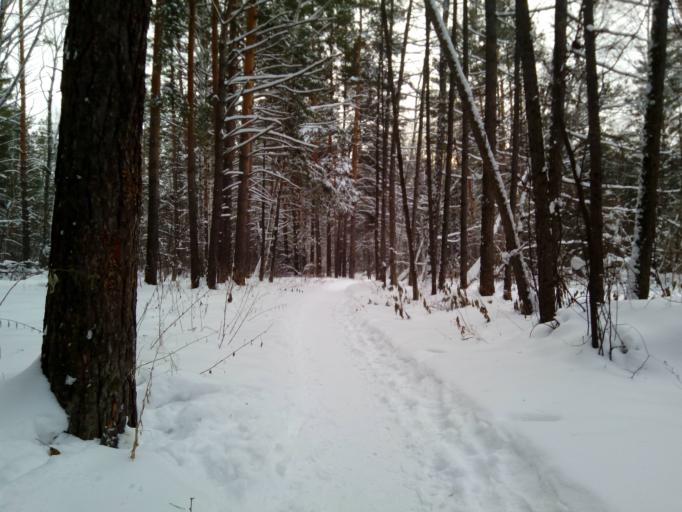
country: RU
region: Novosibirsk
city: Akademgorodok
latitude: 54.8572
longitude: 83.0928
